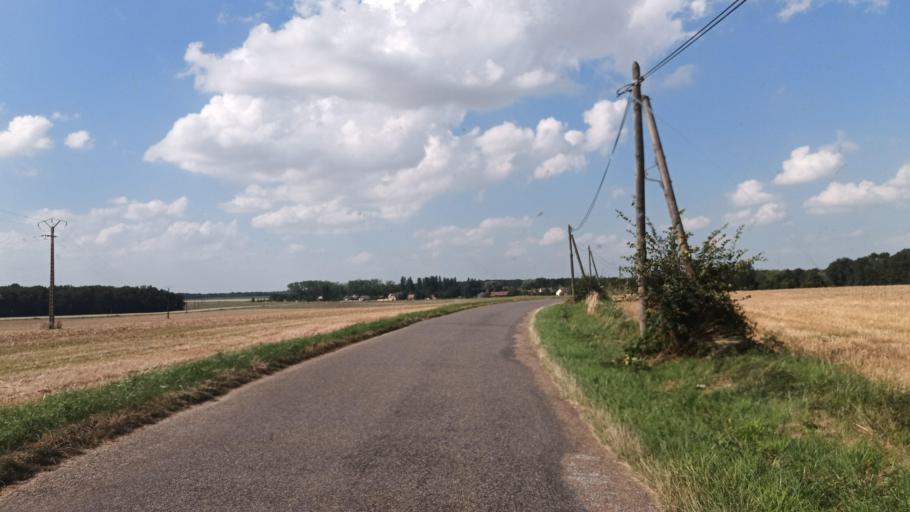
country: FR
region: Bourgogne
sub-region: Departement de l'Yonne
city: Saint-Valerien
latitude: 48.1388
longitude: 3.0895
